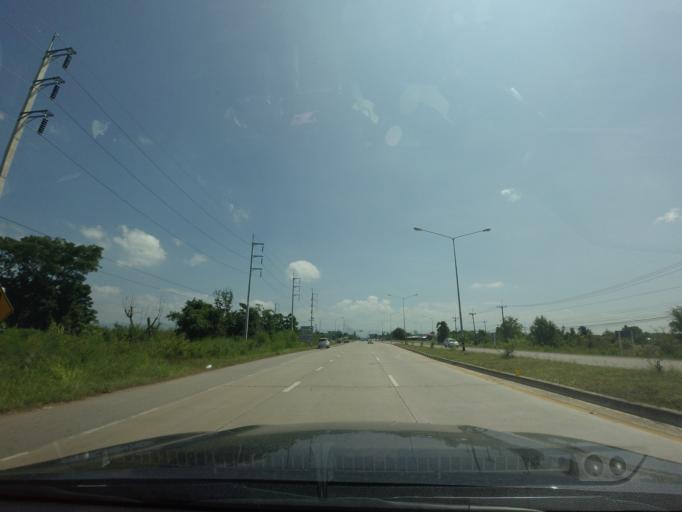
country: TH
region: Phetchabun
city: Lom Sak
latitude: 16.7662
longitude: 101.1840
